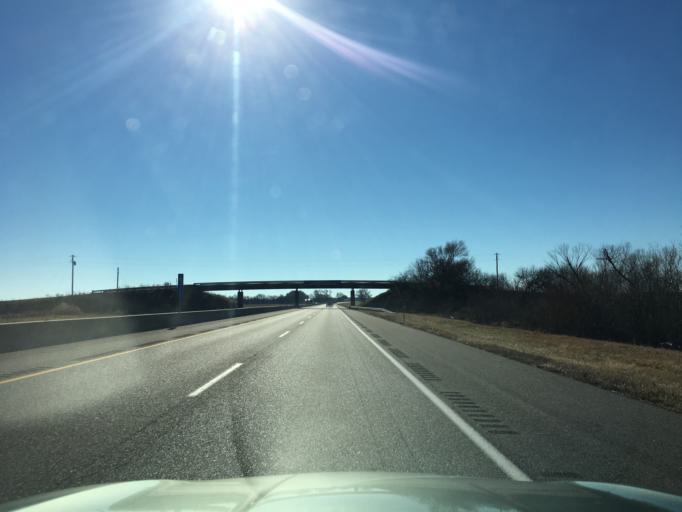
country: US
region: Kansas
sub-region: Sumner County
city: Belle Plaine
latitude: 37.4227
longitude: -97.3213
